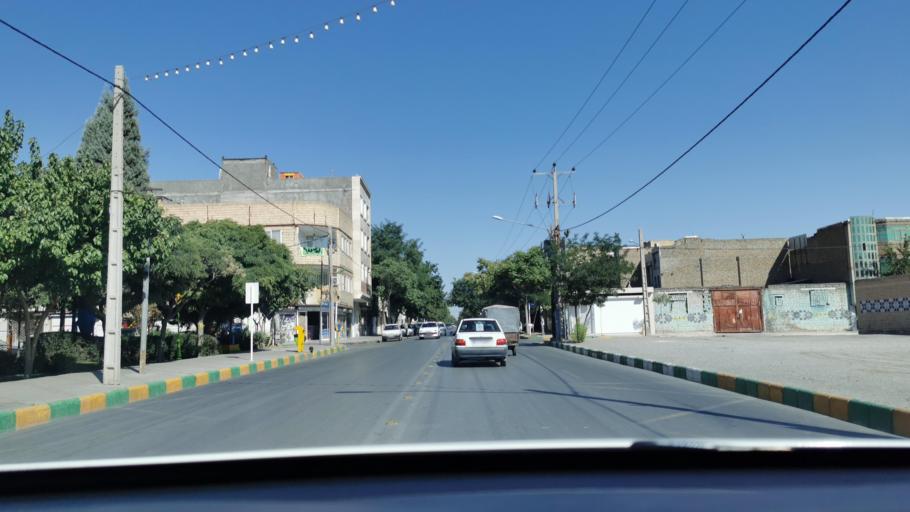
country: IR
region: Razavi Khorasan
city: Mashhad
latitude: 36.3348
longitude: 59.6385
